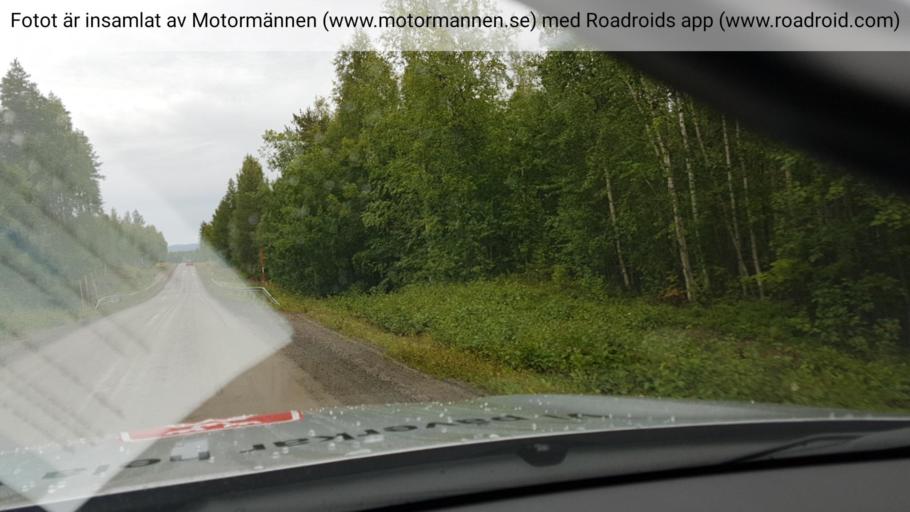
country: SE
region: Norrbotten
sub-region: Alvsbyns Kommun
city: AElvsbyn
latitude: 65.9407
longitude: 21.2343
